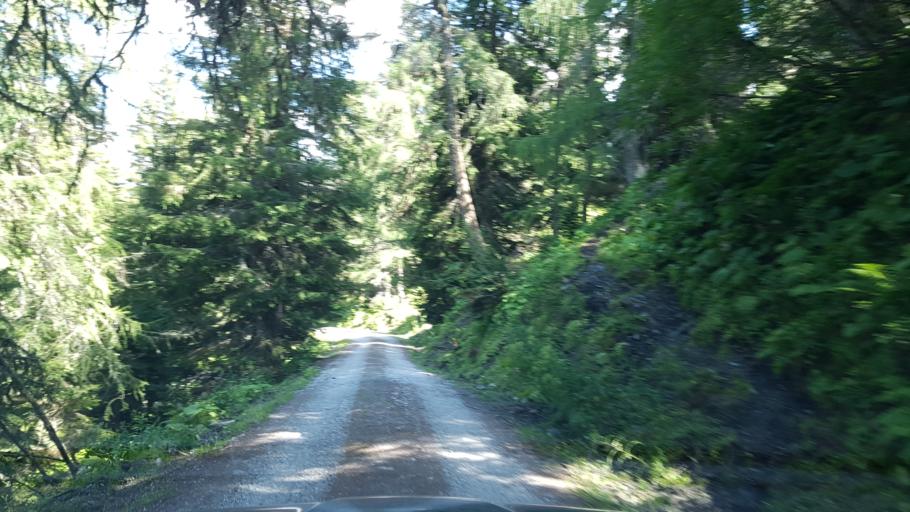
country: AT
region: Salzburg
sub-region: Politischer Bezirk Sankt Johann im Pongau
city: Dorfgastein
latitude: 47.2418
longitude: 13.0638
